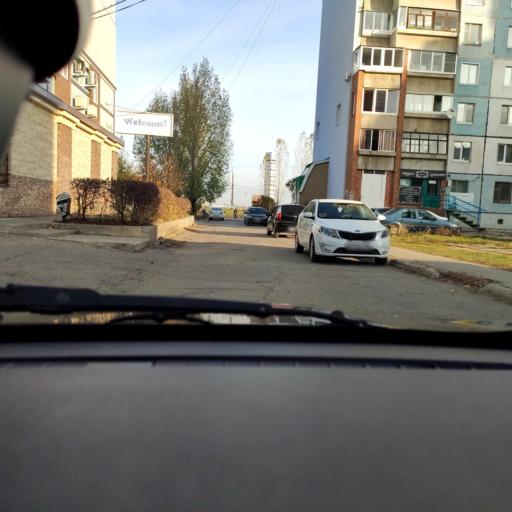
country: RU
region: Samara
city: Tol'yatti
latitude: 53.5473
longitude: 49.3412
